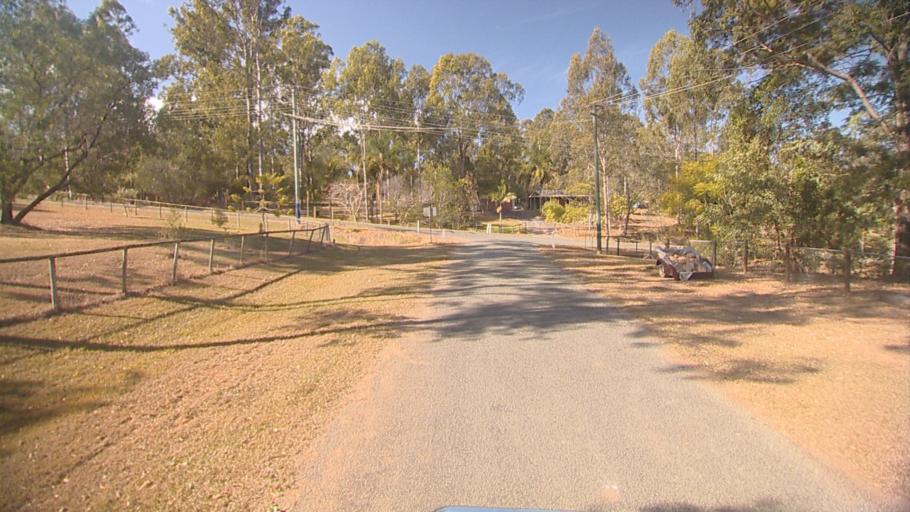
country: AU
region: Queensland
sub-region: Logan
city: Cedar Vale
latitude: -27.8557
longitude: 152.9844
